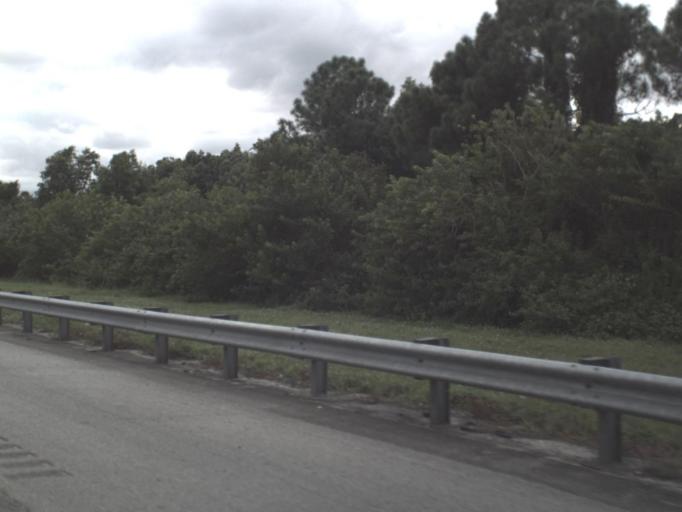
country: US
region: Florida
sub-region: Palm Beach County
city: Limestone Creek
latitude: 26.8948
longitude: -80.1364
